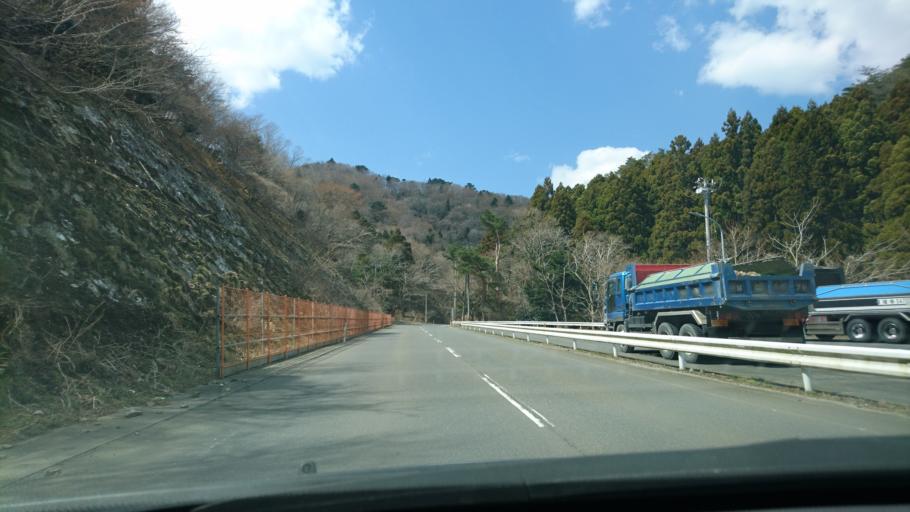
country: JP
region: Miyagi
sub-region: Oshika Gun
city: Onagawa Cho
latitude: 38.4542
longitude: 141.4886
